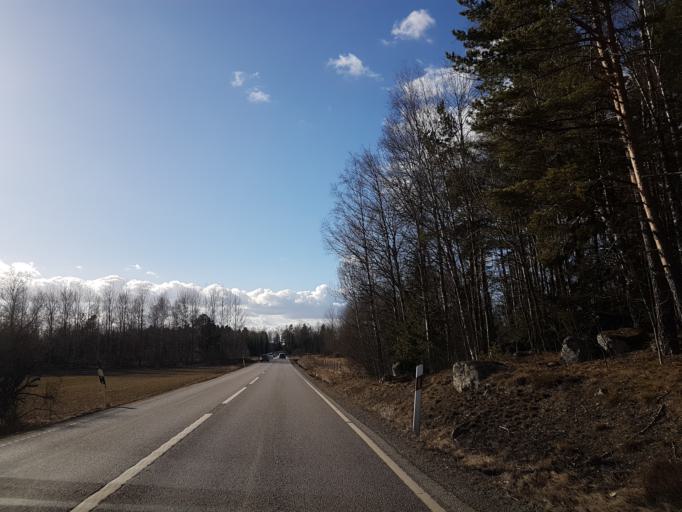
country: SE
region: Stockholm
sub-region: Norrtalje Kommun
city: Rimbo
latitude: 59.7371
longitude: 18.4652
